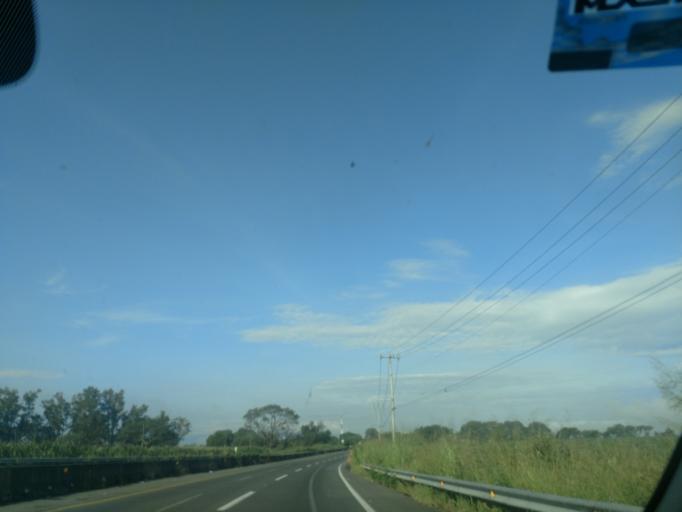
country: MX
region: Jalisco
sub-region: Ameca
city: Los Pocitos
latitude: 20.5382
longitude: -103.9266
